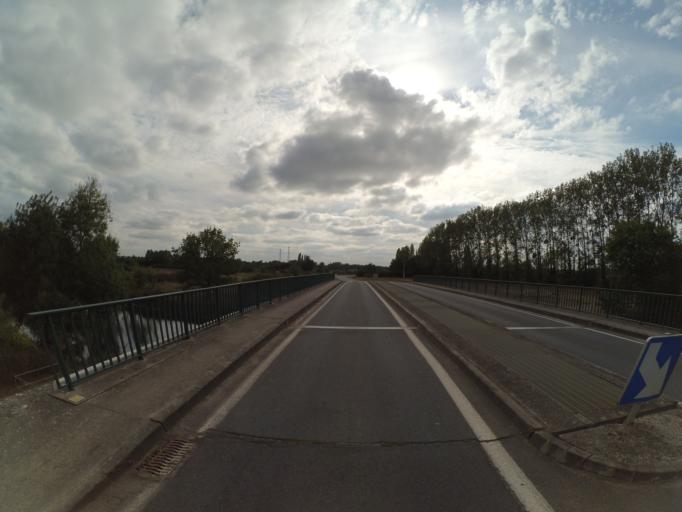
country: FR
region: Centre
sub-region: Departement d'Indre-et-Loire
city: Montlouis-sur-Loire
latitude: 47.4075
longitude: 0.8228
